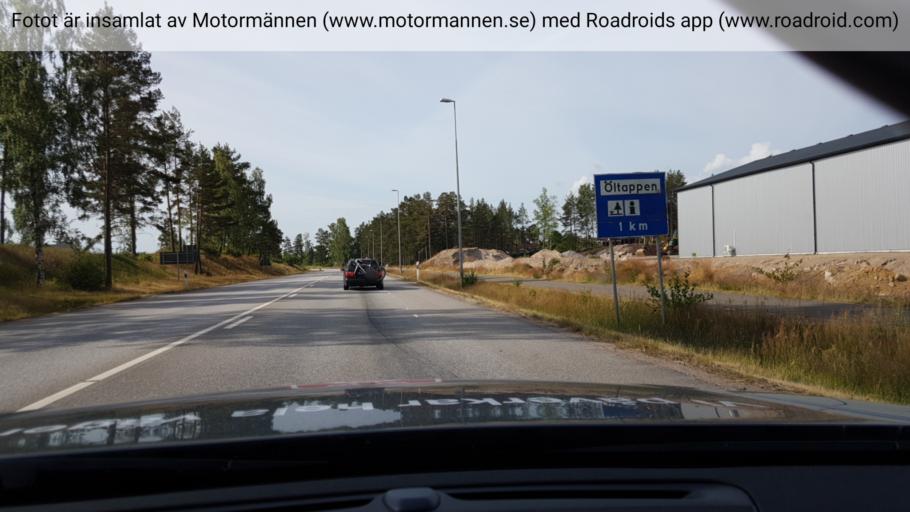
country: SE
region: Vaestra Goetaland
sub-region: Karlsborgs Kommun
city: Karlsborg
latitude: 58.5516
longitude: 14.4999
